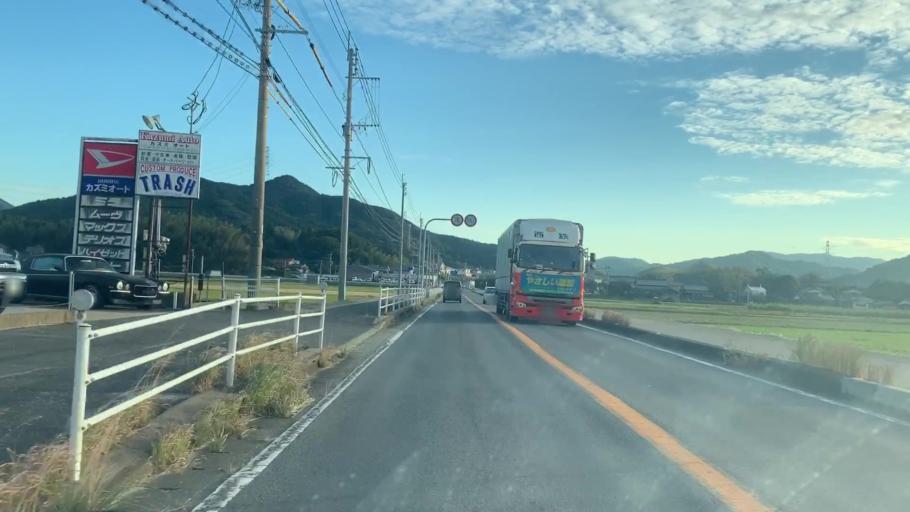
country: JP
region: Saga Prefecture
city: Karatsu
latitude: 33.4027
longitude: 129.9867
